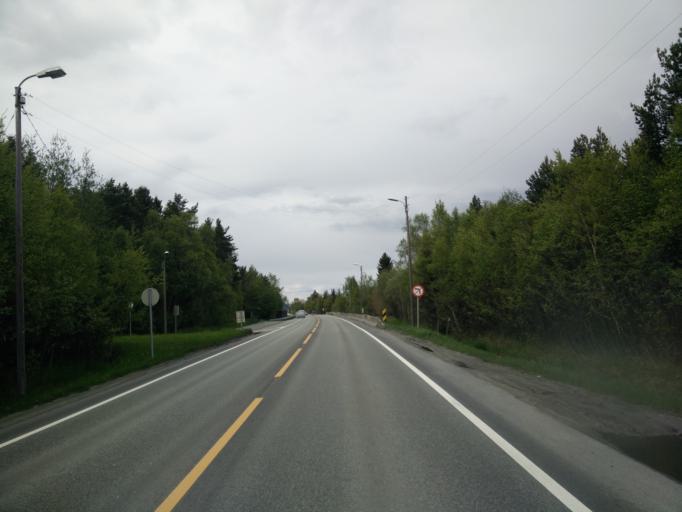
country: NO
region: Sor-Trondelag
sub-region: Trondheim
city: Trondheim
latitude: 63.3465
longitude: 10.3688
